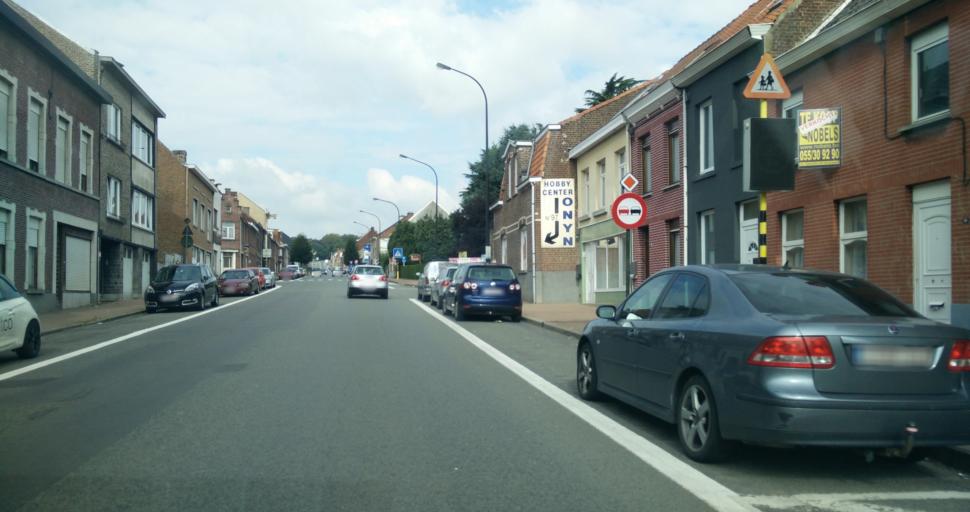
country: BE
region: Flanders
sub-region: Provincie Oost-Vlaanderen
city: Ronse
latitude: 50.7522
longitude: 3.5951
